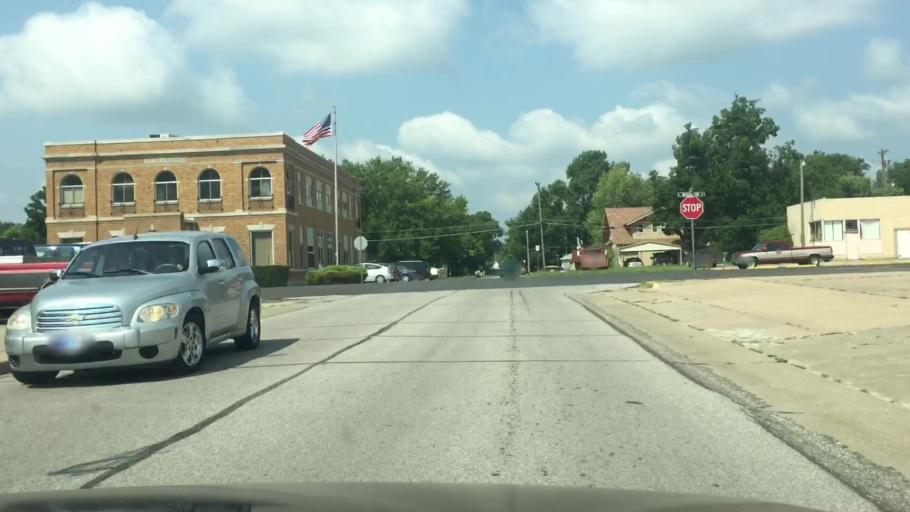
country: US
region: Kansas
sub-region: Allen County
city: Iola
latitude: 37.9200
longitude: -95.4051
